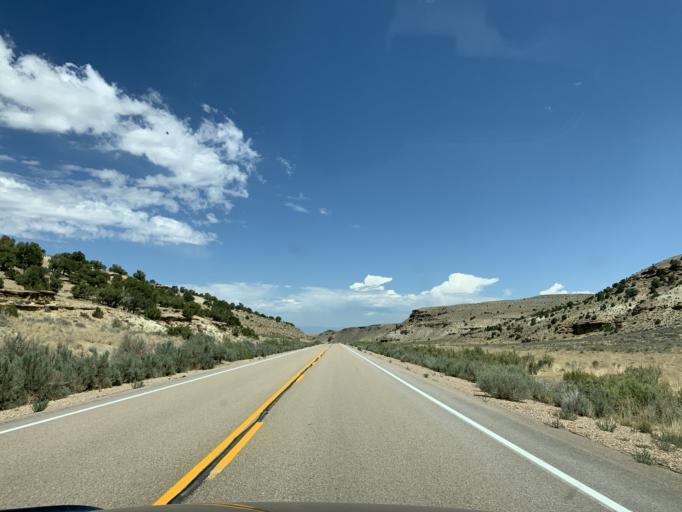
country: US
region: Utah
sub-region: Duchesne County
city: Duchesne
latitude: 39.9928
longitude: -110.1553
